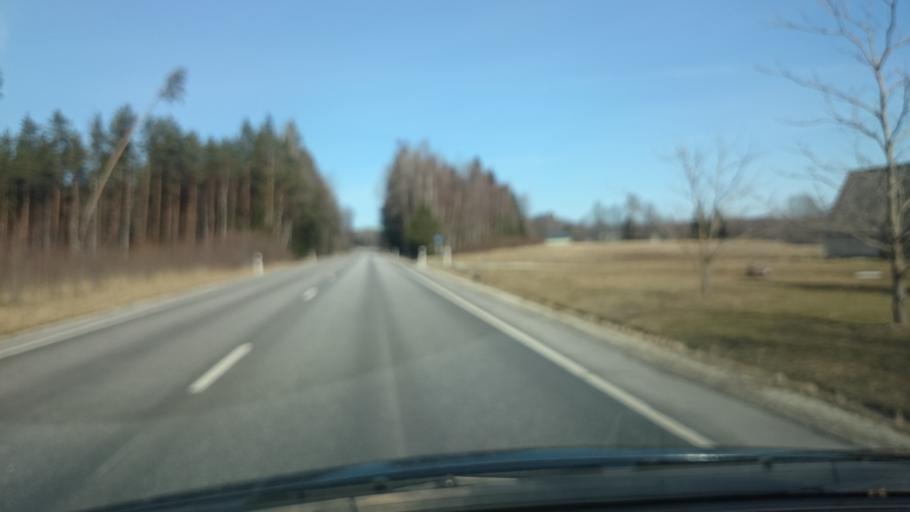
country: EE
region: Jaervamaa
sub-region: Tueri vald
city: Sarevere
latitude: 58.7101
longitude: 25.2682
